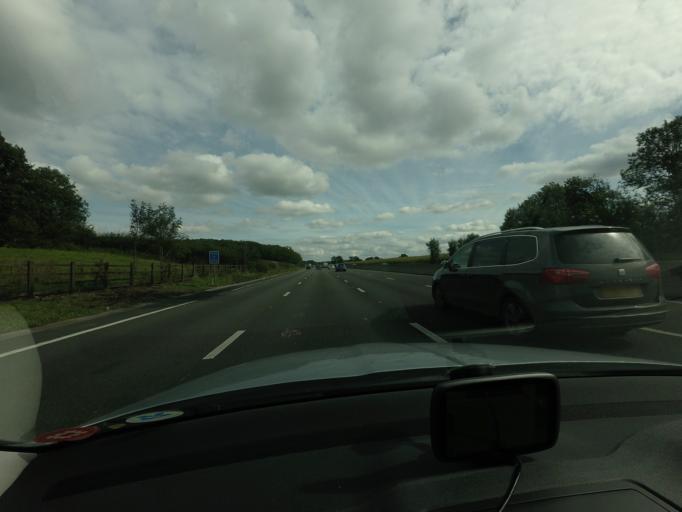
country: GB
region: England
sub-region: Kent
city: Westerham
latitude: 51.2786
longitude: 0.0894
